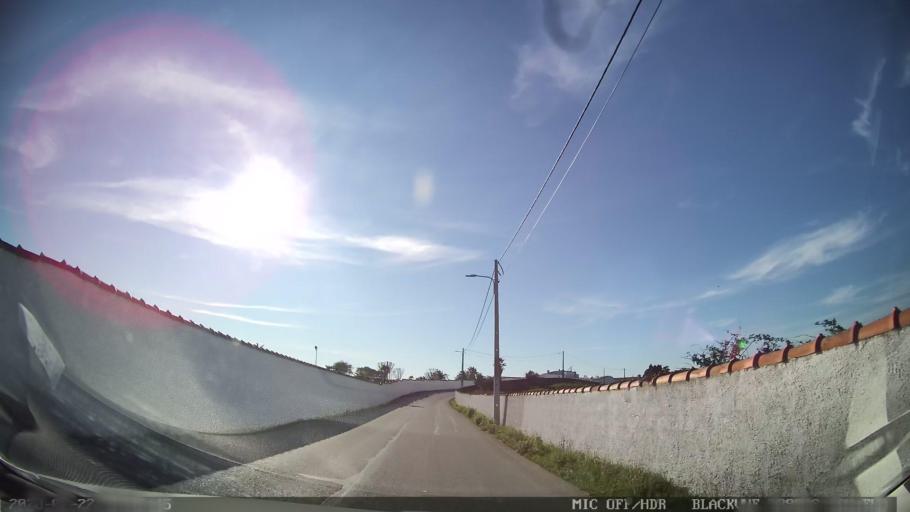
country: PT
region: Lisbon
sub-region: Vila Franca de Xira
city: Vila Franca de Xira
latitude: 38.9703
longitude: -8.9967
